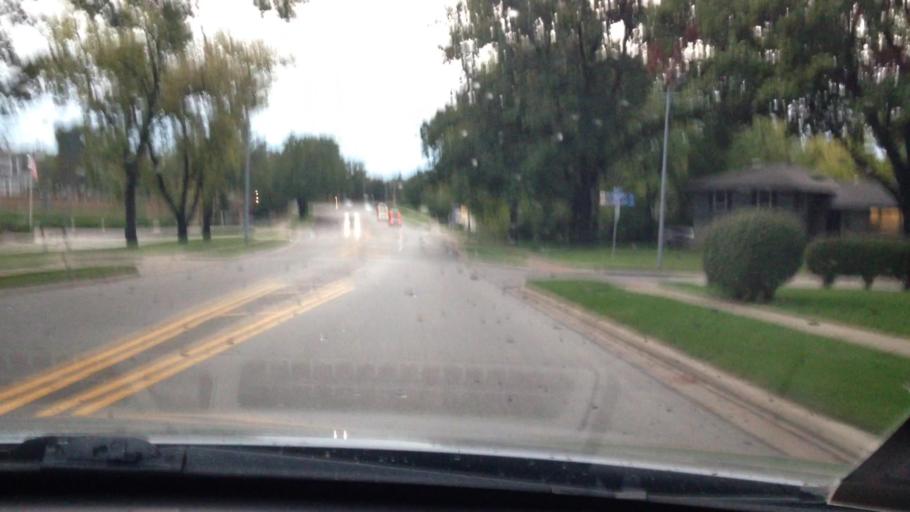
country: US
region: Kansas
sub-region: Johnson County
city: Prairie Village
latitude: 38.9825
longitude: -94.6258
